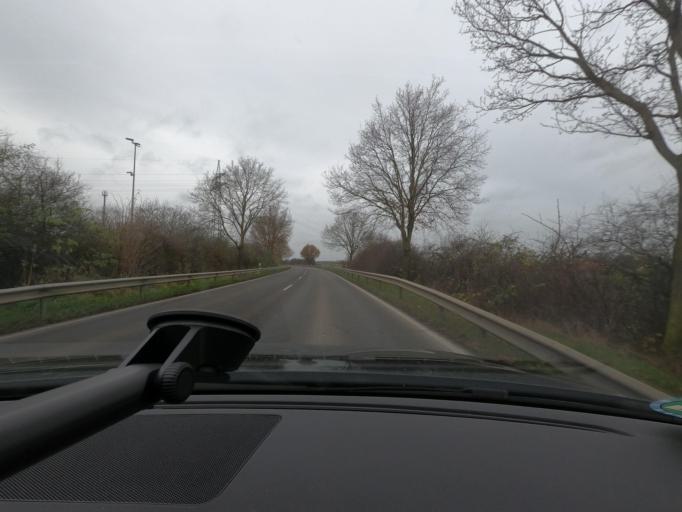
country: DE
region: North Rhine-Westphalia
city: Kempen
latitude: 51.3756
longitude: 6.4378
